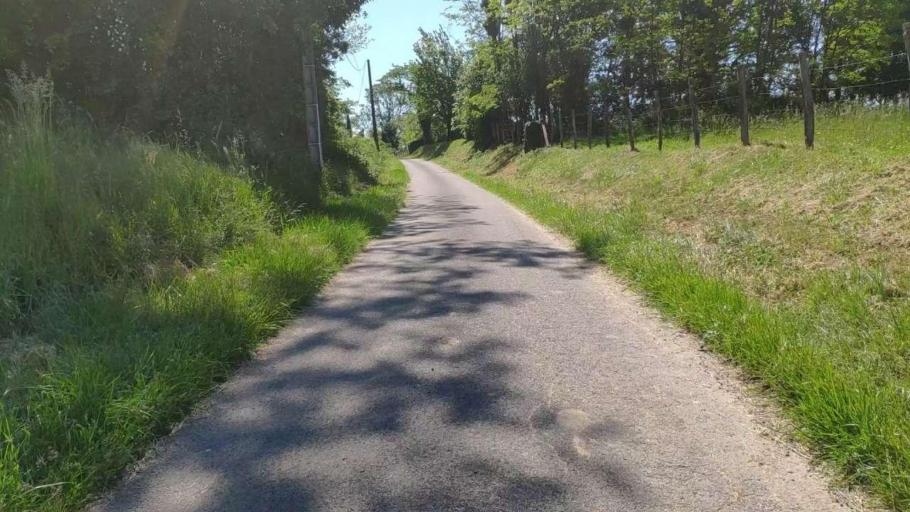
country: FR
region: Franche-Comte
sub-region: Departement du Jura
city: Bletterans
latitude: 46.7807
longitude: 5.4250
